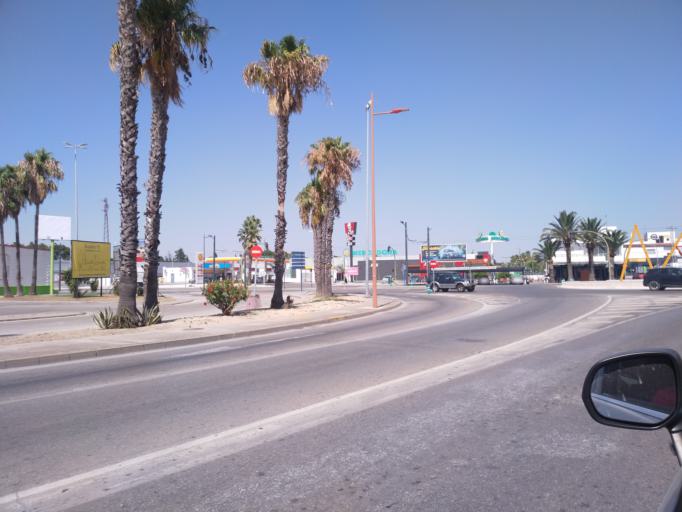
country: ES
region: Andalusia
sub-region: Provincia de Cadiz
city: Chiclana de la Frontera
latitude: 36.4296
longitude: -6.1437
